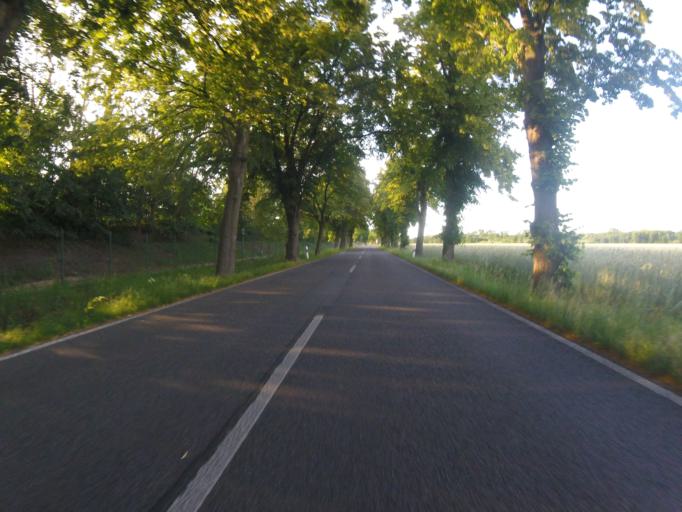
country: DE
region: Brandenburg
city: Mittenwalde
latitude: 52.2280
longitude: 13.5482
